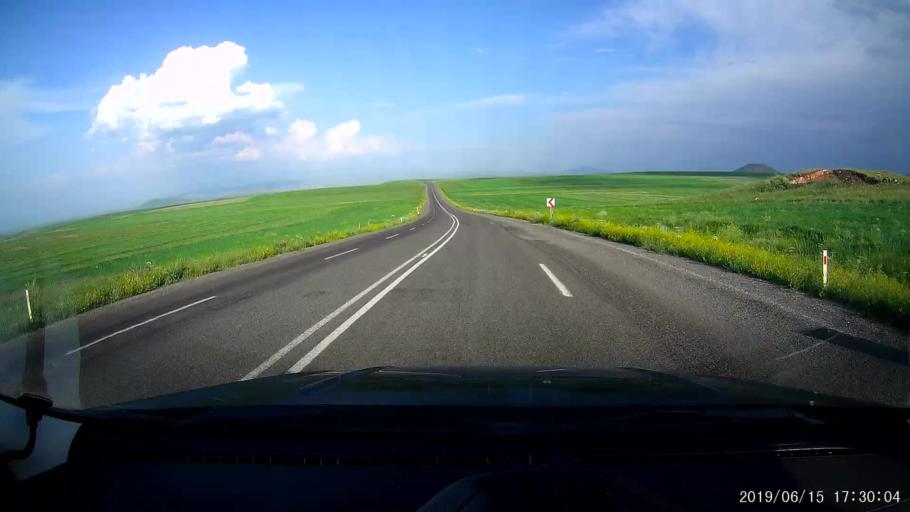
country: TR
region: Kars
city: Basgedikler
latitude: 40.5848
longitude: 43.4627
